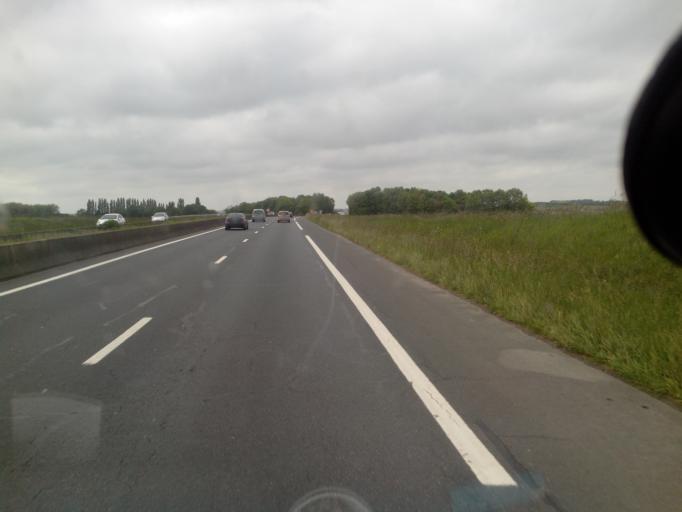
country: FR
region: Lower Normandy
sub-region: Departement du Calvados
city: Bretteville-sur-Odon
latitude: 49.1705
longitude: -0.4293
